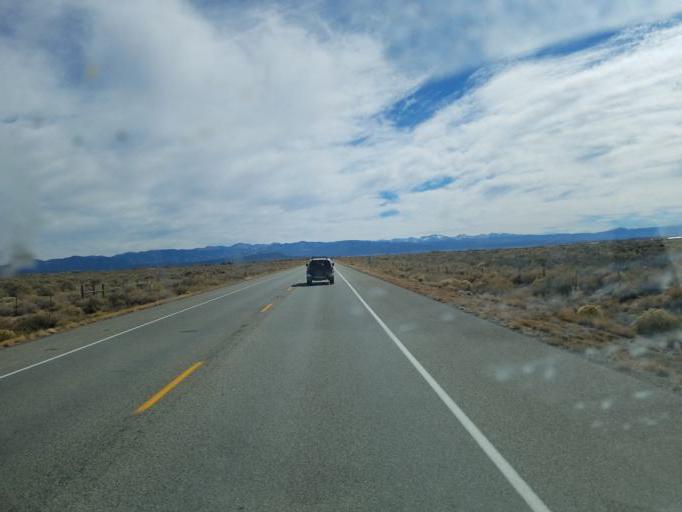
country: US
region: Colorado
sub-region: Costilla County
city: San Luis
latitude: 37.4486
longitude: -105.5401
